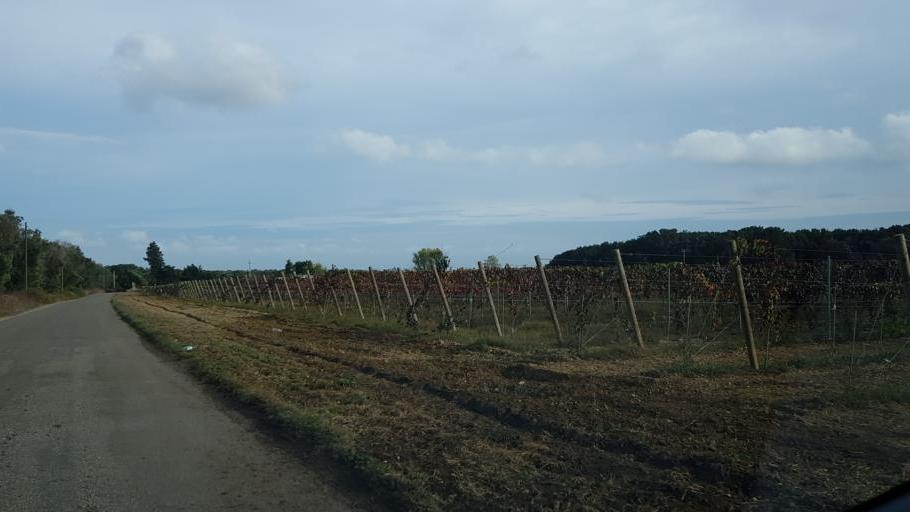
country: IT
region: Apulia
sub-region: Provincia di Brindisi
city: Oria
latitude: 40.5010
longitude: 17.6667
